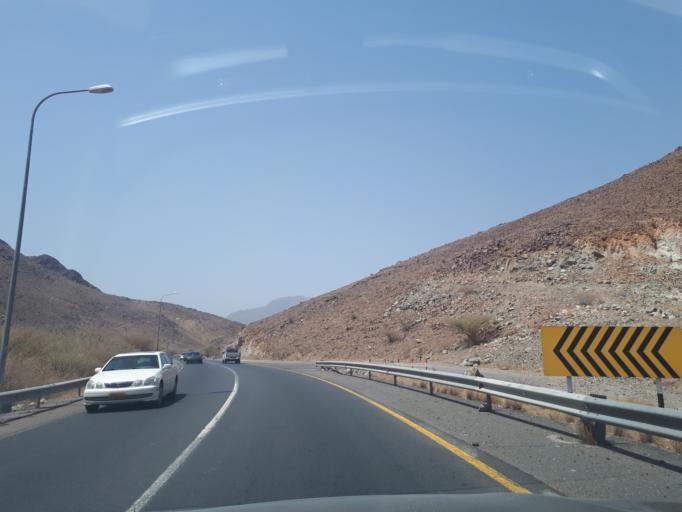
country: OM
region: Muhafazat ad Dakhiliyah
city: Sufalat Sama'il
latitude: 23.2474
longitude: 58.0873
